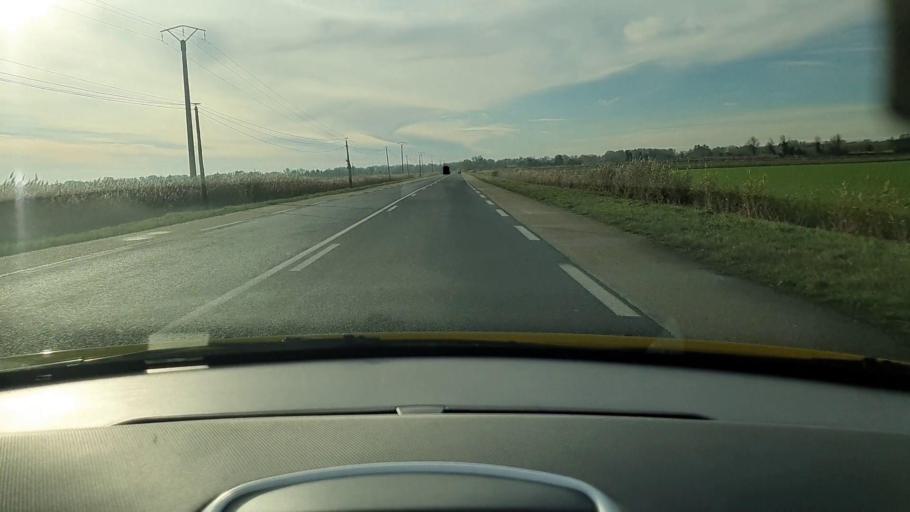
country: FR
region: Languedoc-Roussillon
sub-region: Departement du Gard
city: Bellegarde
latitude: 43.7195
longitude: 4.5482
